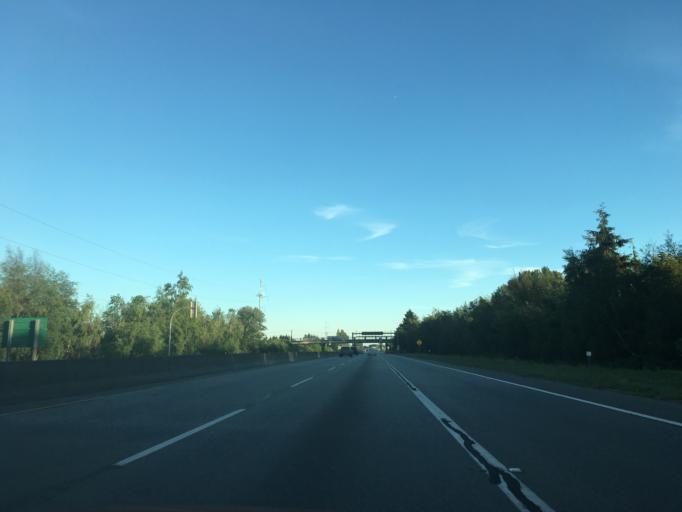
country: CA
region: British Columbia
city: Richmond
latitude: 49.1583
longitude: -123.0868
